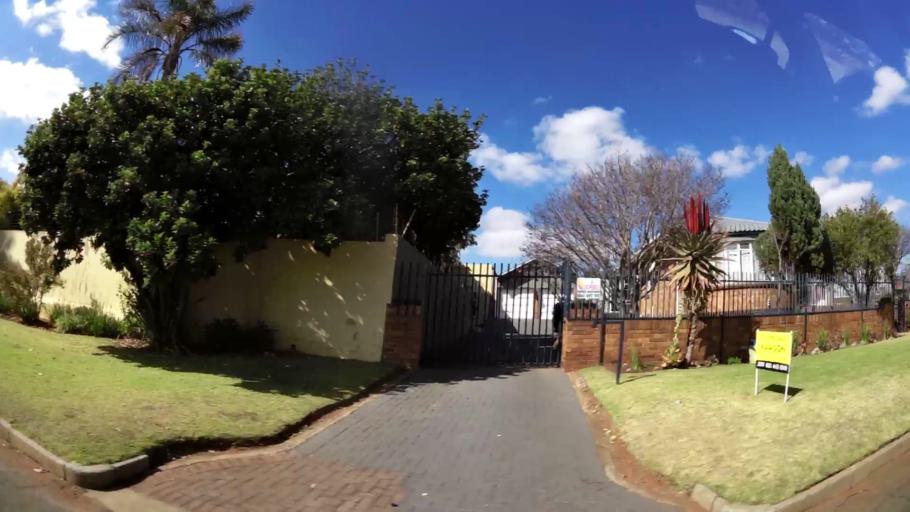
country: ZA
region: Gauteng
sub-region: West Rand District Municipality
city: Krugersdorp
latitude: -26.0935
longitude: 27.7835
